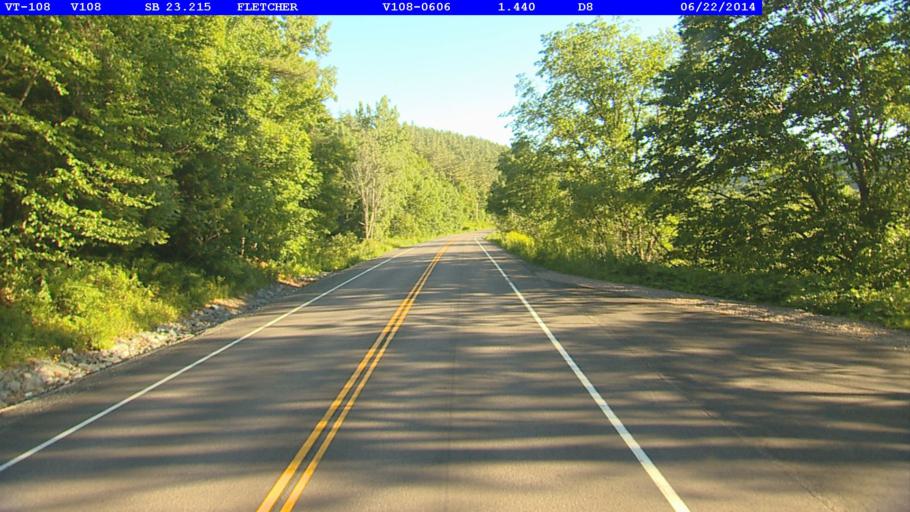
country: US
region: Vermont
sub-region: Lamoille County
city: Johnson
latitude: 44.7210
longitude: -72.8308
